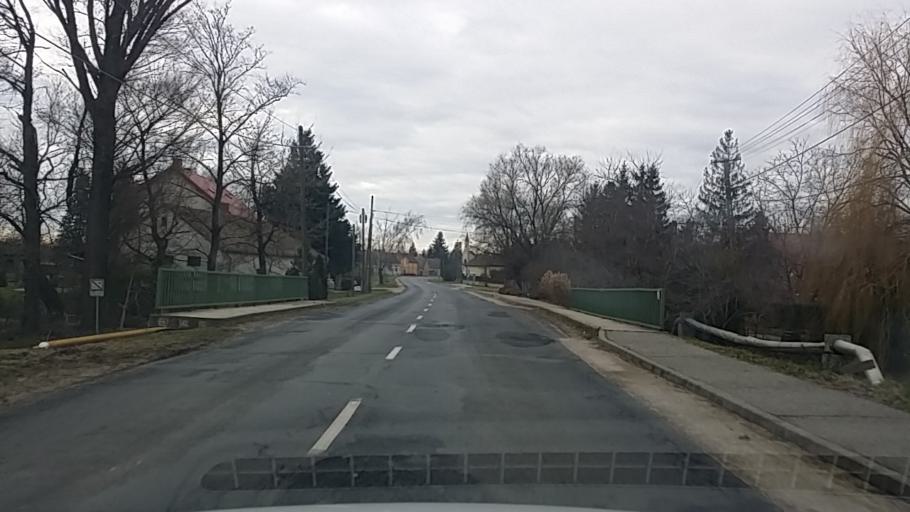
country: HU
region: Vas
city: Celldomolk
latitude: 47.2724
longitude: 17.3067
